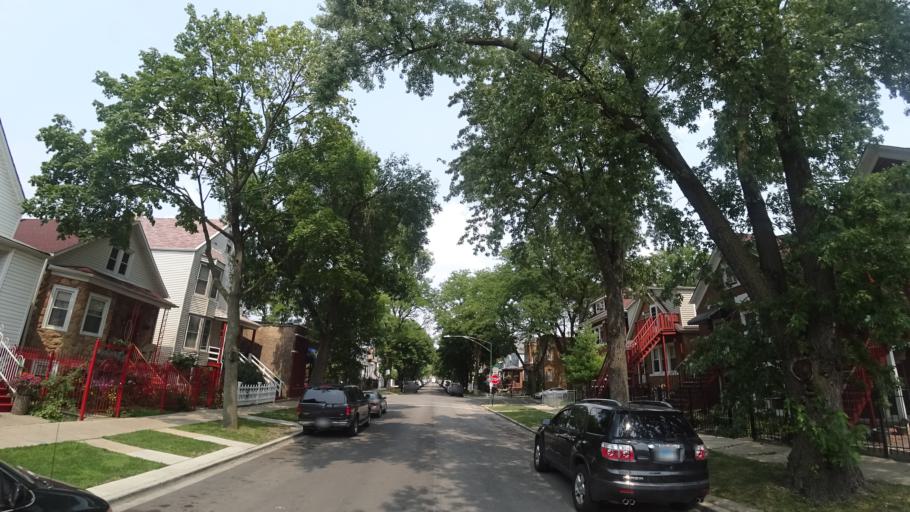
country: US
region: Illinois
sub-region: Cook County
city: Cicero
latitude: 41.8400
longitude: -87.7305
